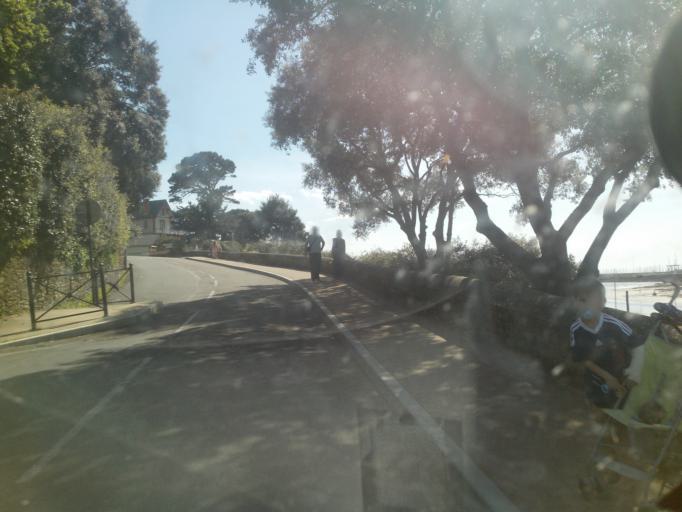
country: FR
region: Pays de la Loire
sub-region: Departement de la Loire-Atlantique
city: Pornic
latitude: 47.1131
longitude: -2.1035
